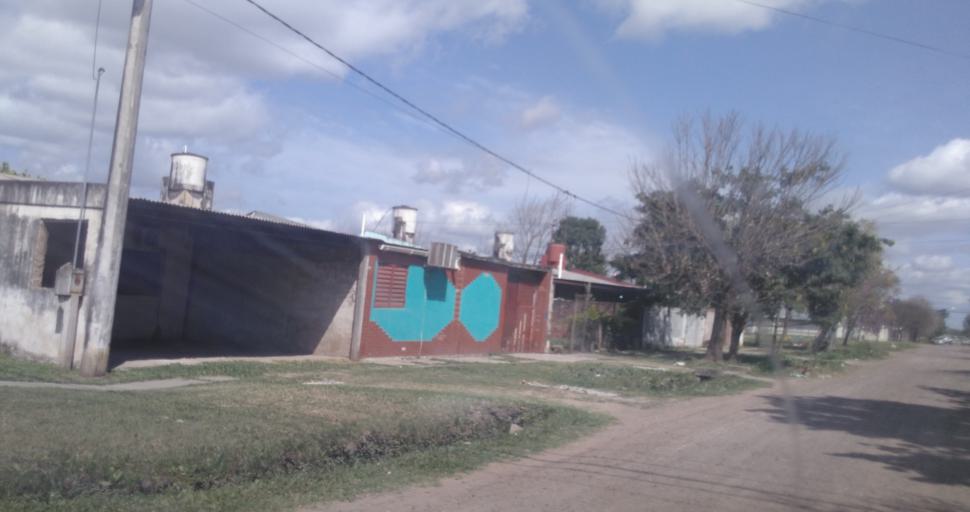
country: AR
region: Chaco
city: Fontana
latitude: -27.4299
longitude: -59.0346
